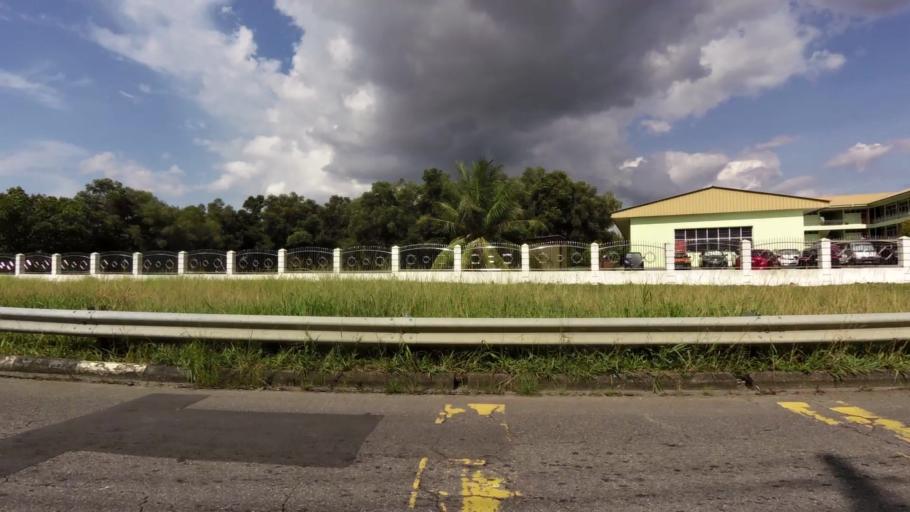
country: BN
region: Brunei and Muara
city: Bandar Seri Begawan
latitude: 4.9622
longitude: 114.9565
